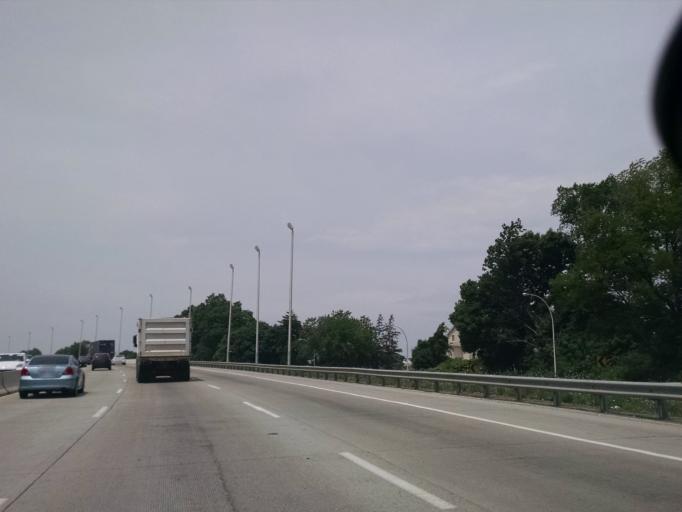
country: US
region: New York
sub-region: Richmond County
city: Staten Island
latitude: 40.6113
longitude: -74.1139
